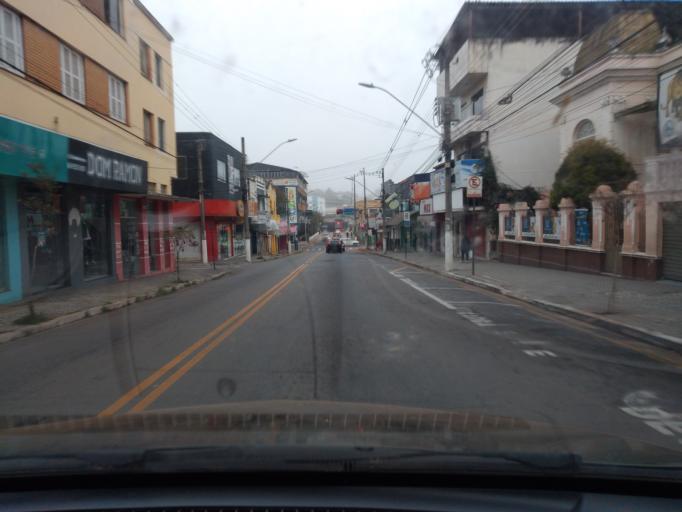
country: BR
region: Minas Gerais
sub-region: Tres Coracoes
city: Tres Coracoes
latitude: -21.6990
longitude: -45.2576
